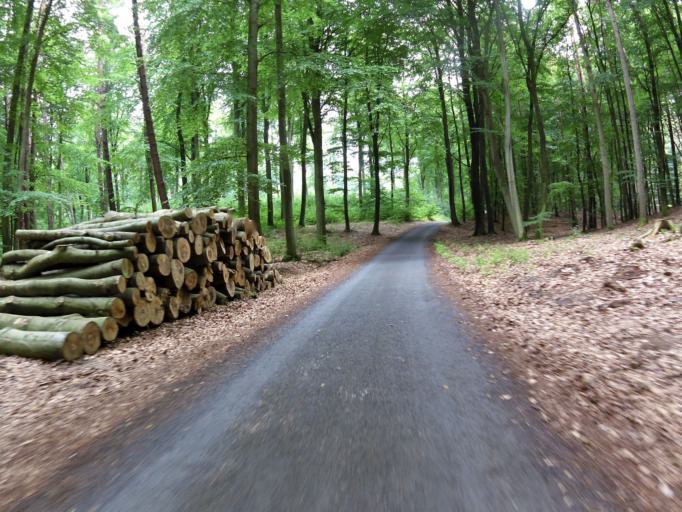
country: DE
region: Mecklenburg-Vorpommern
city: Seebad Heringsdorf
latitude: 53.9251
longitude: 14.1710
